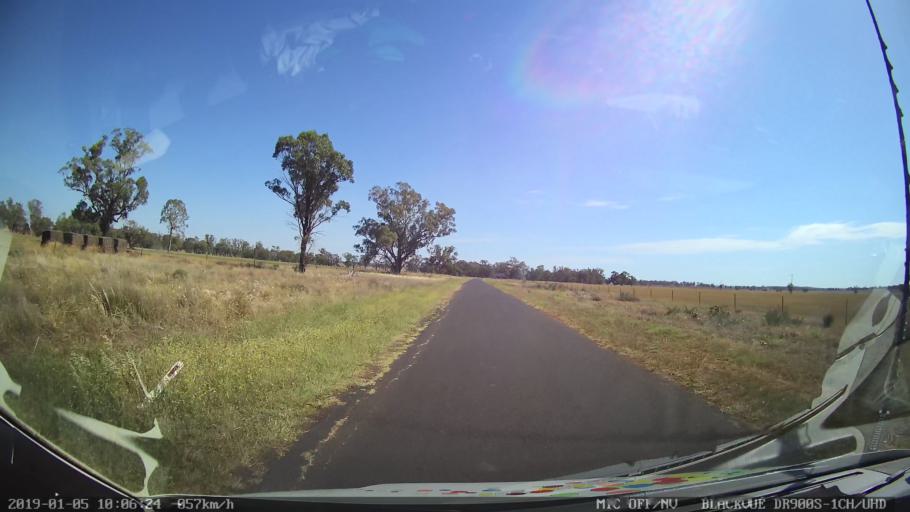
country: AU
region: New South Wales
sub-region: Gilgandra
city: Gilgandra
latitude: -31.6583
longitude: 148.8696
